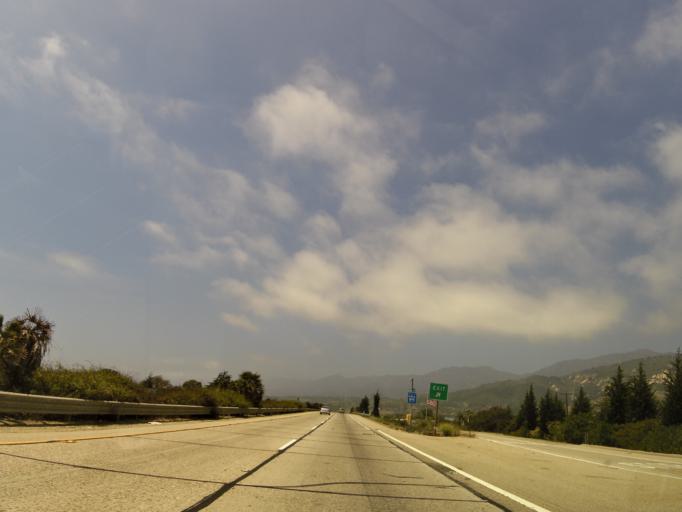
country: US
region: California
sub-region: Santa Barbara County
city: Toro Canyon
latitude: 34.4088
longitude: -119.5500
